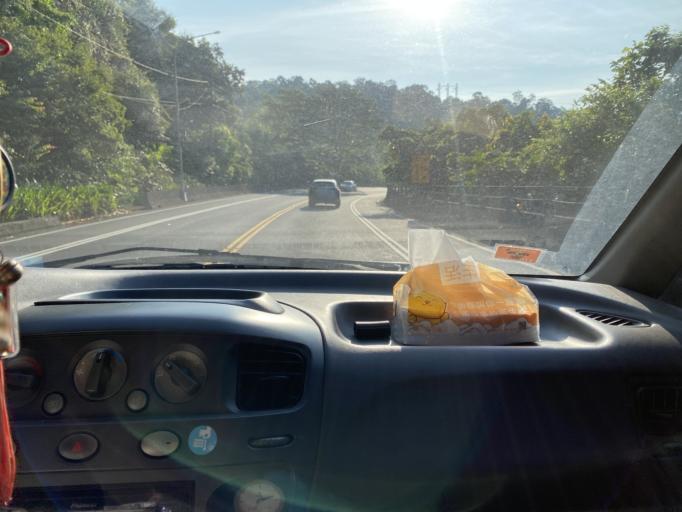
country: TW
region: Taiwan
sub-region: Keelung
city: Keelung
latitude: 25.0192
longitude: 121.7949
